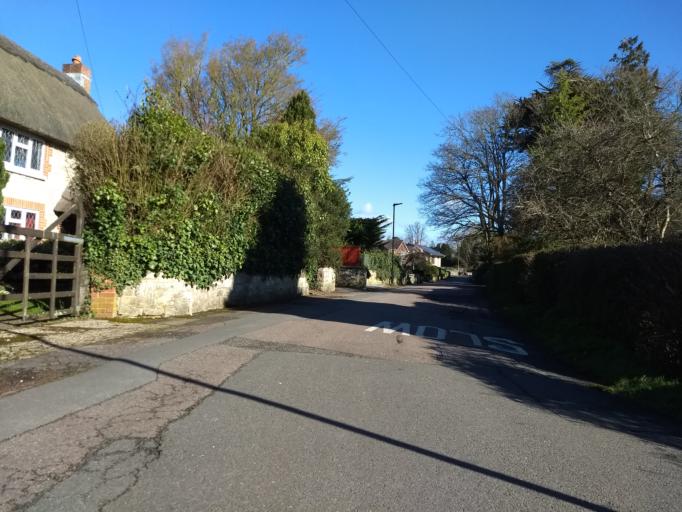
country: GB
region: England
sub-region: Isle of Wight
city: Ryde
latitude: 50.7296
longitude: -1.1863
